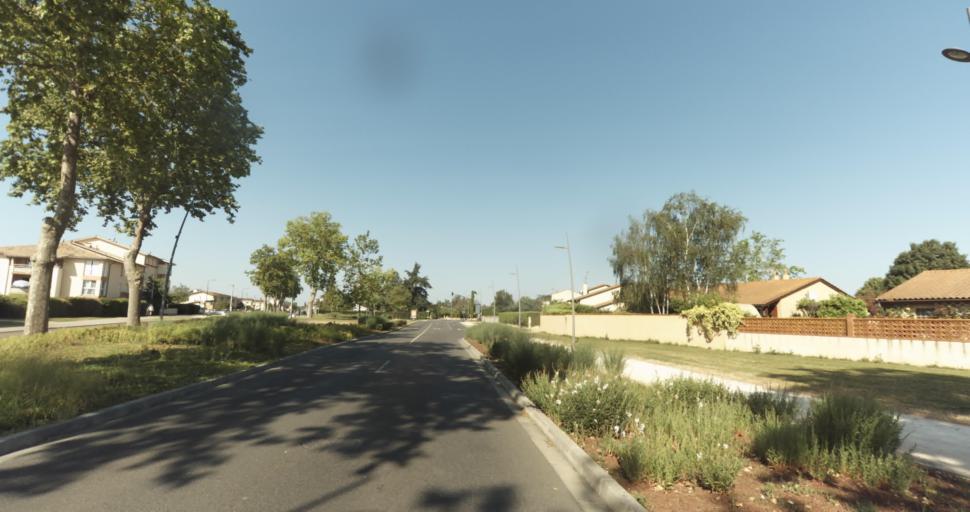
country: FR
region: Midi-Pyrenees
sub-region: Departement de la Haute-Garonne
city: Plaisance-du-Touch
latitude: 43.5688
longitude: 1.3046
